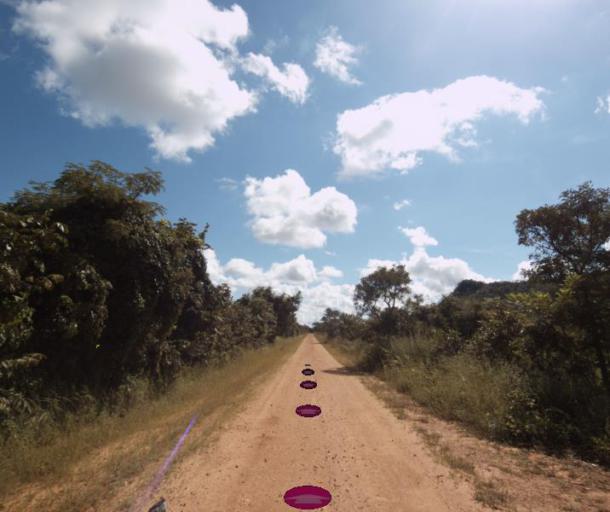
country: BR
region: Goias
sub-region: Pirenopolis
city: Pirenopolis
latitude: -15.7744
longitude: -49.0002
